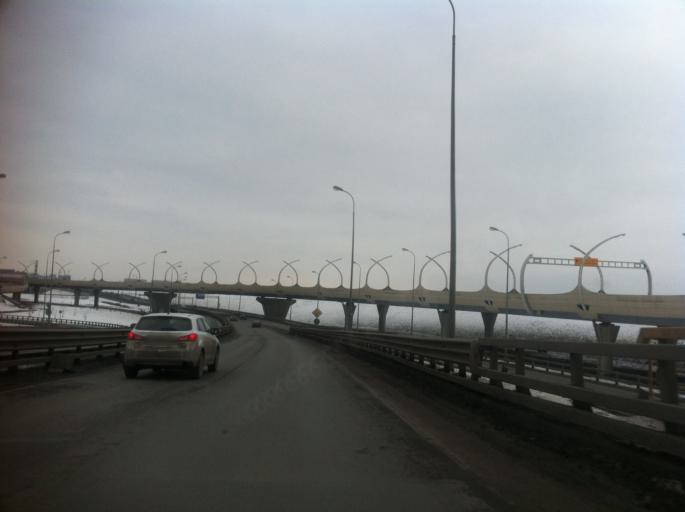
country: RU
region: St.-Petersburg
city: Dachnoye
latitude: 59.8336
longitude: 30.2709
